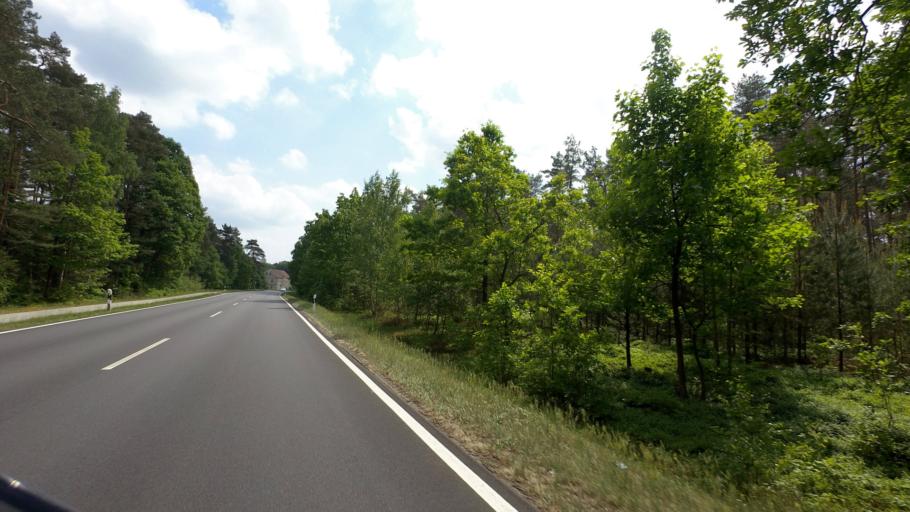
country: DE
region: Saxony
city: Niesky
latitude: 51.3388
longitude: 14.8102
